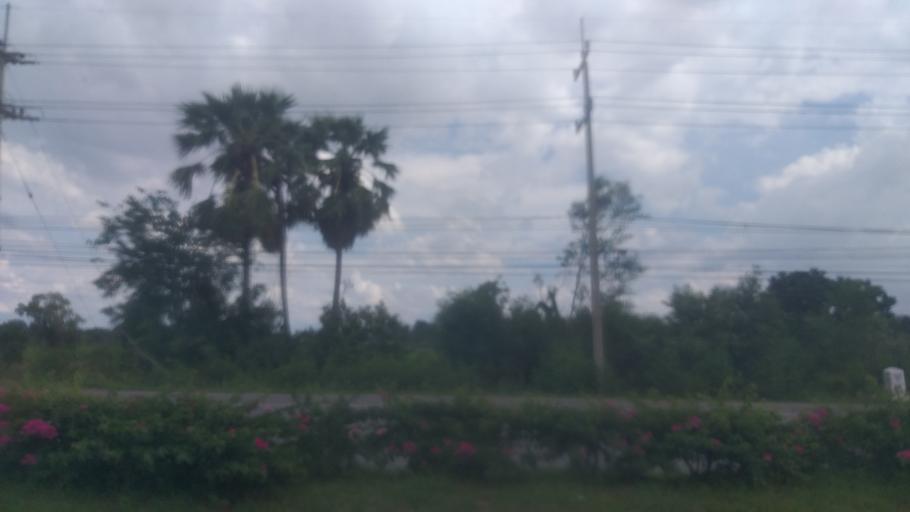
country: TH
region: Chaiyaphum
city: Noen Sa-nga
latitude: 15.6783
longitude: 102.0064
